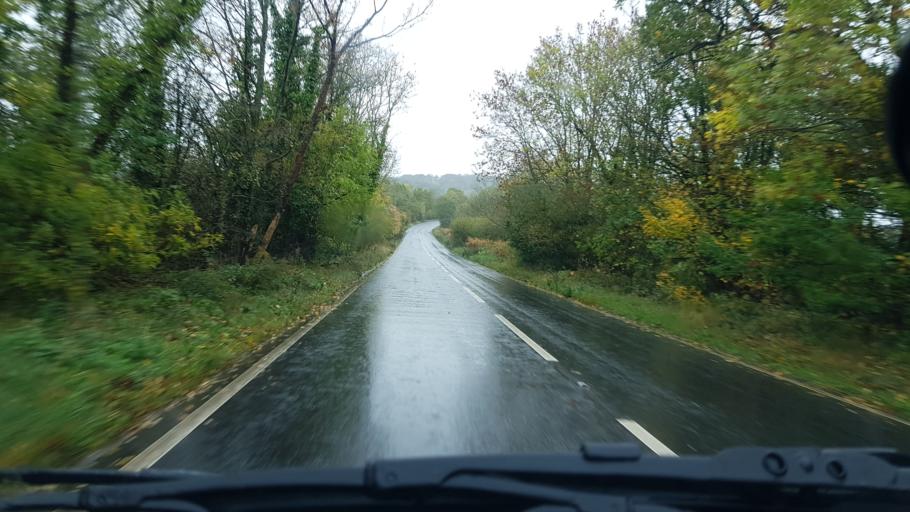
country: GB
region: England
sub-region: Gloucestershire
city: Stow on the Wold
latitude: 51.9086
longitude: -1.7198
